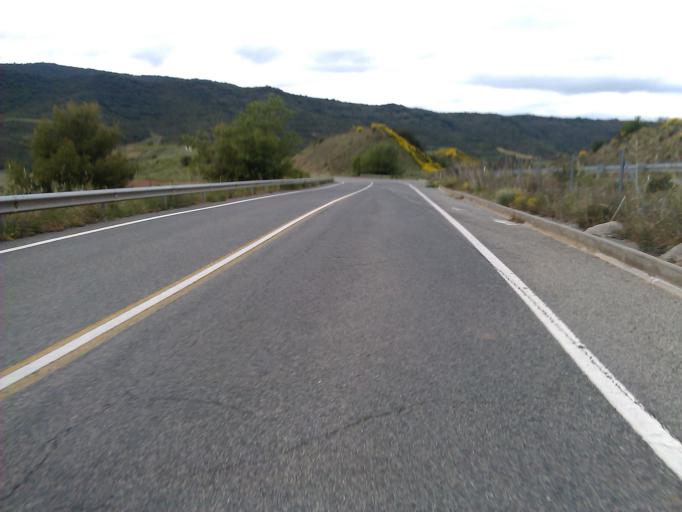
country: ES
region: Navarre
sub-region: Provincia de Navarra
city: Cirauqui
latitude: 42.6758
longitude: -1.9027
